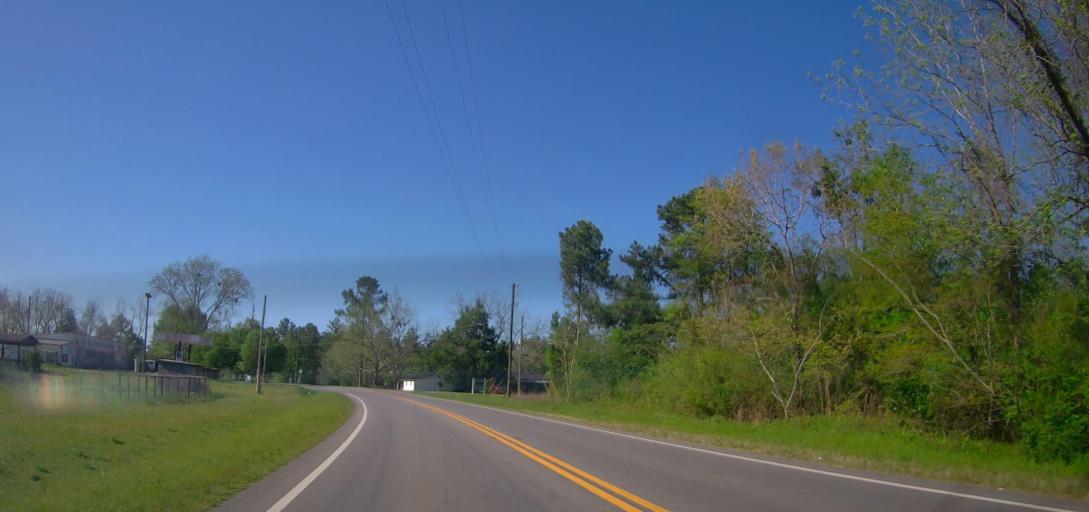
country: US
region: Georgia
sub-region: Pulaski County
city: Hawkinsville
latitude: 32.1289
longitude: -83.5006
